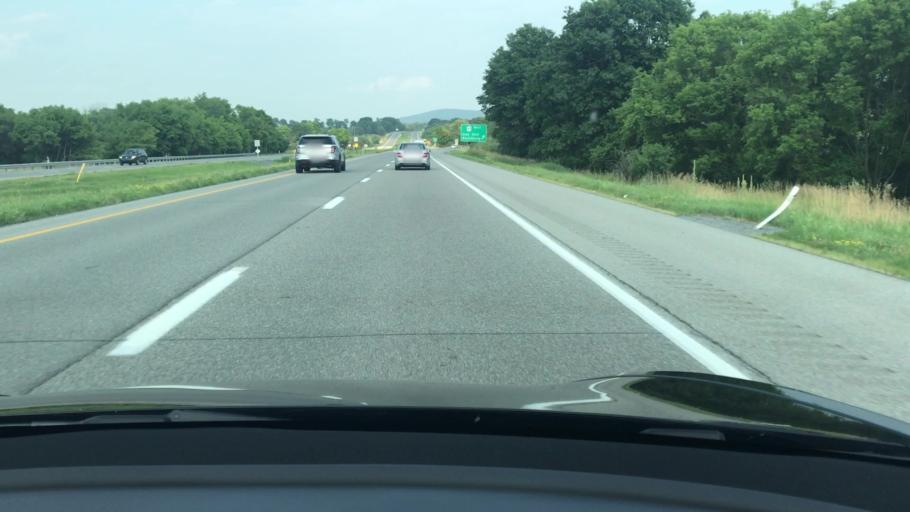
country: US
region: Pennsylvania
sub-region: Centre County
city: Boalsburg
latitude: 40.7892
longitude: -77.8079
